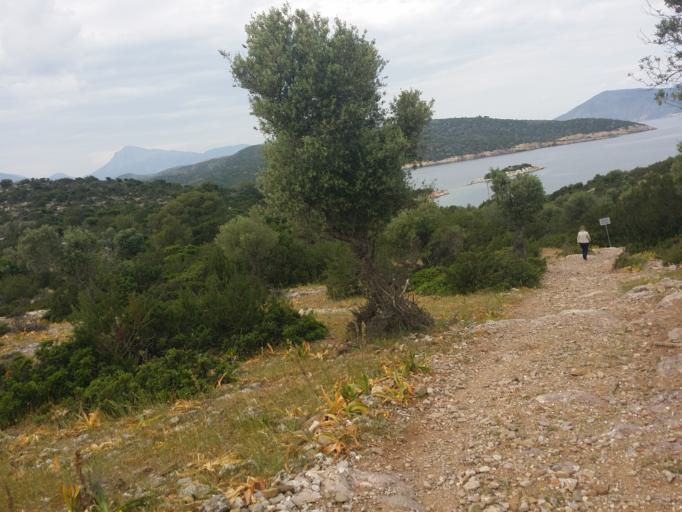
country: GR
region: Attica
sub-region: Nomos Piraios
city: Galatas
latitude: 37.5200
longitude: 23.4296
